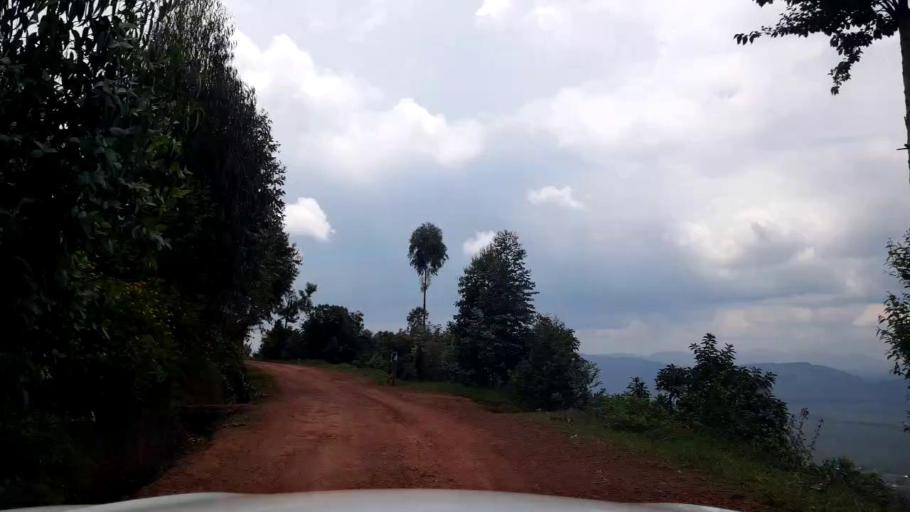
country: RW
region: Northern Province
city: Byumba
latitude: -1.4883
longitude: 29.9292
